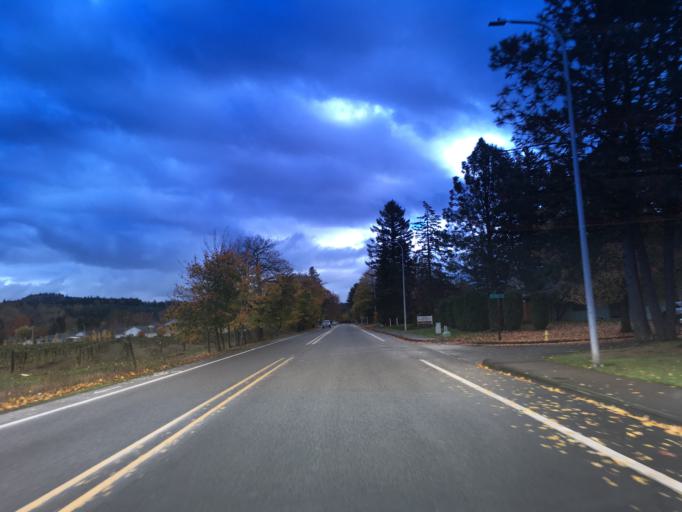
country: US
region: Oregon
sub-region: Multnomah County
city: Troutdale
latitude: 45.5190
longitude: -122.3836
